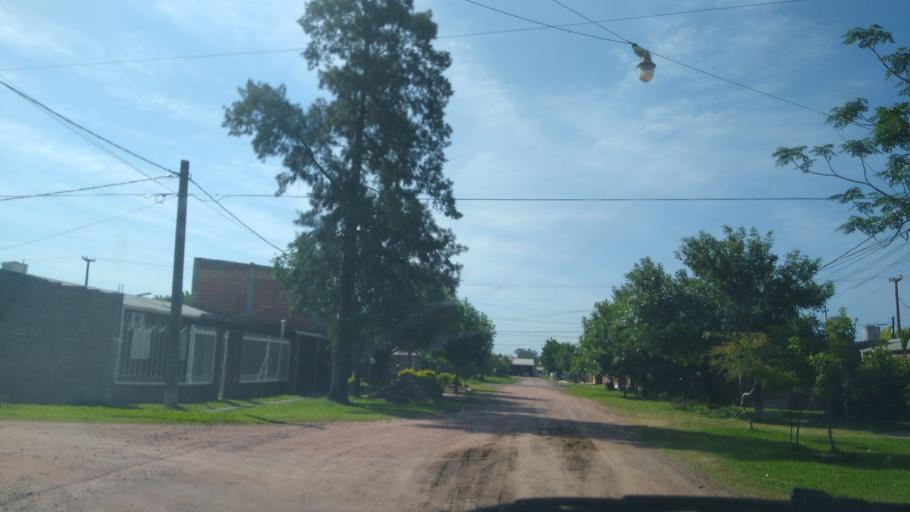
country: AR
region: Chaco
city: Barranqueras
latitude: -27.4949
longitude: -58.9612
